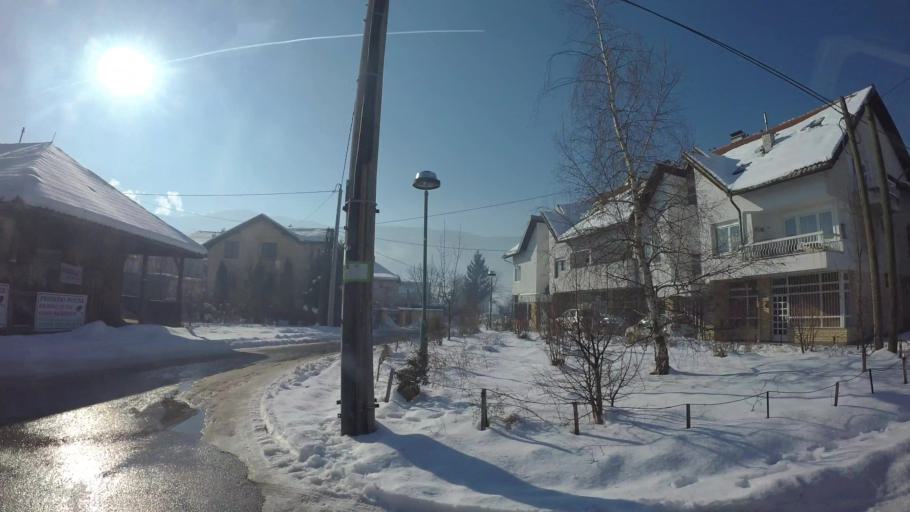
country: BA
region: Federation of Bosnia and Herzegovina
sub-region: Kanton Sarajevo
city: Sarajevo
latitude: 43.8147
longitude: 18.3130
